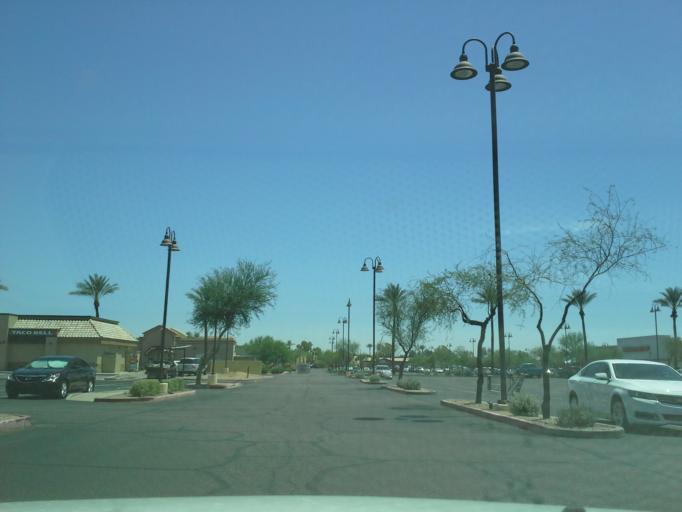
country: US
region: Arizona
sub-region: Maricopa County
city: Scottsdale
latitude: 33.5788
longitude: -111.8873
